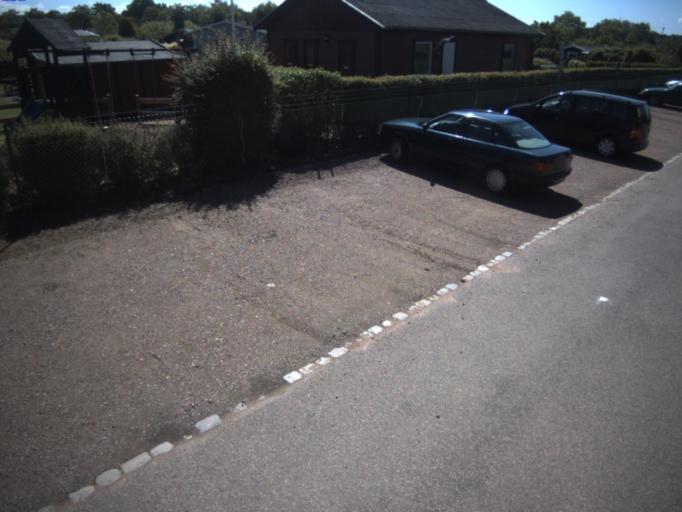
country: SE
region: Skane
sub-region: Helsingborg
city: Helsingborg
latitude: 56.0732
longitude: 12.7017
